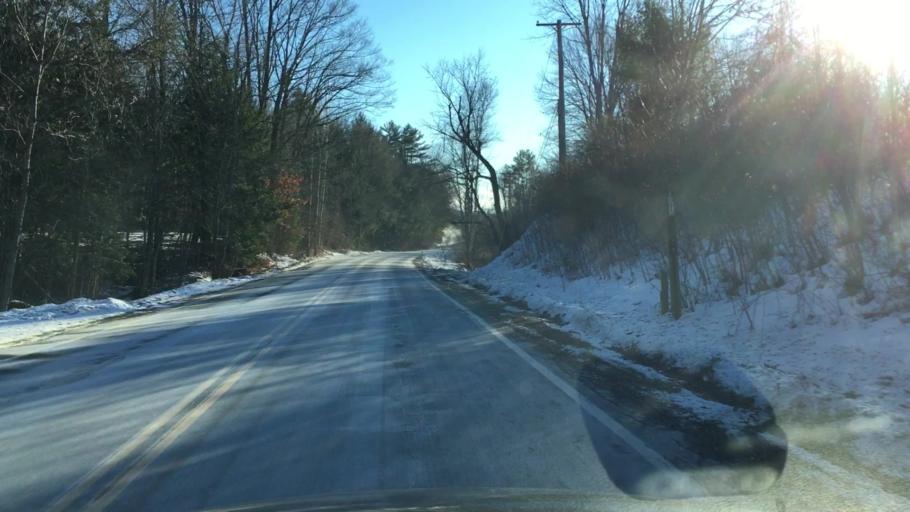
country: US
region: New Hampshire
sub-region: Grafton County
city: Woodsville
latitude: 44.2327
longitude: -72.0451
